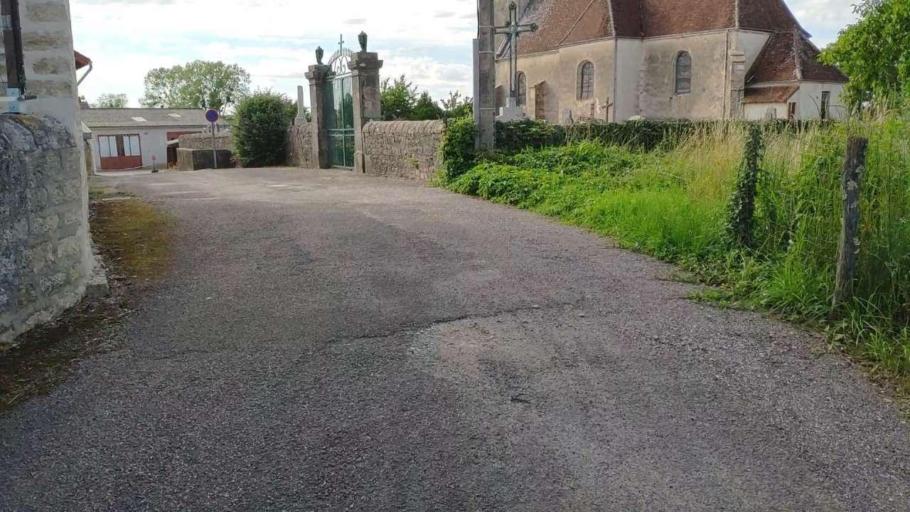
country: FR
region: Franche-Comte
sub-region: Departement du Jura
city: Bletterans
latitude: 46.8260
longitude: 5.5334
